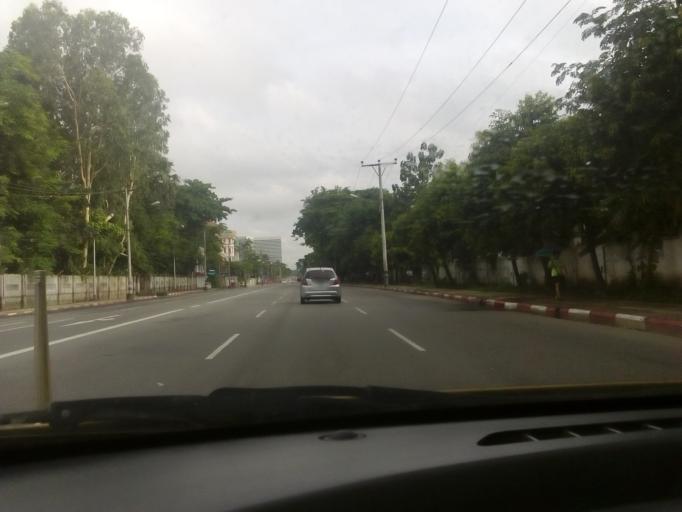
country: MM
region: Yangon
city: Yangon
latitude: 16.8423
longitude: 96.1564
